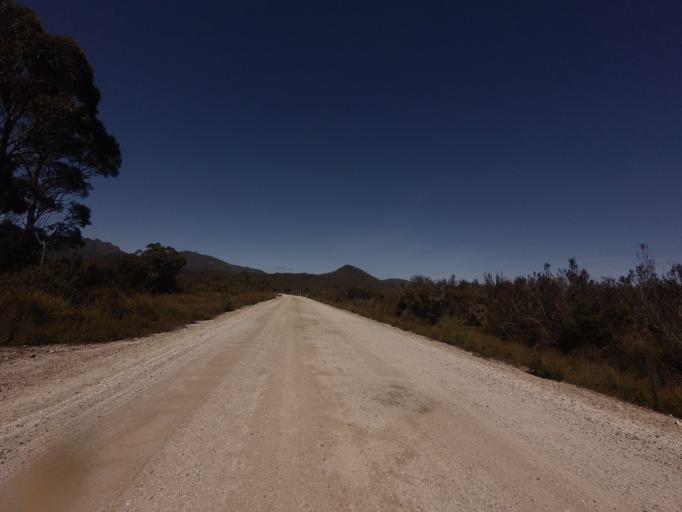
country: AU
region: Tasmania
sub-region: Huon Valley
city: Geeveston
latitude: -42.8927
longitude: 146.3749
